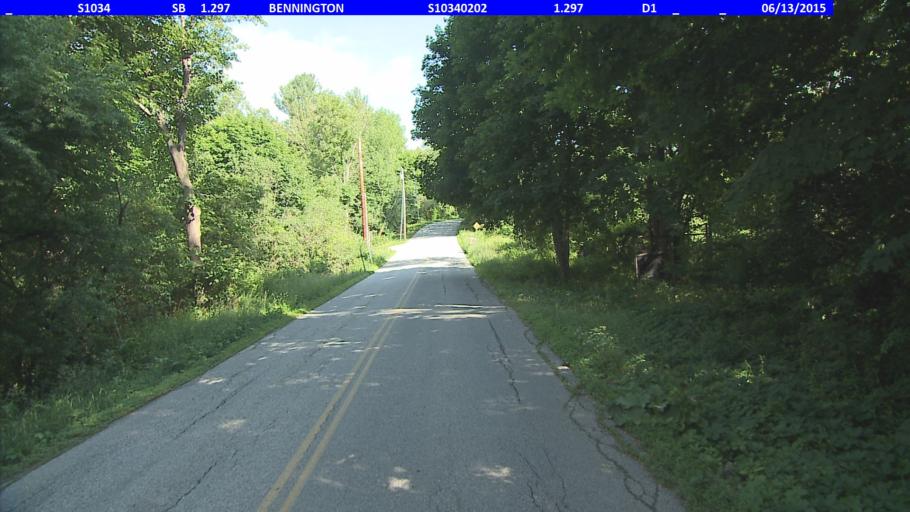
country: US
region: Vermont
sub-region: Bennington County
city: Bennington
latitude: 42.8696
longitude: -73.2102
